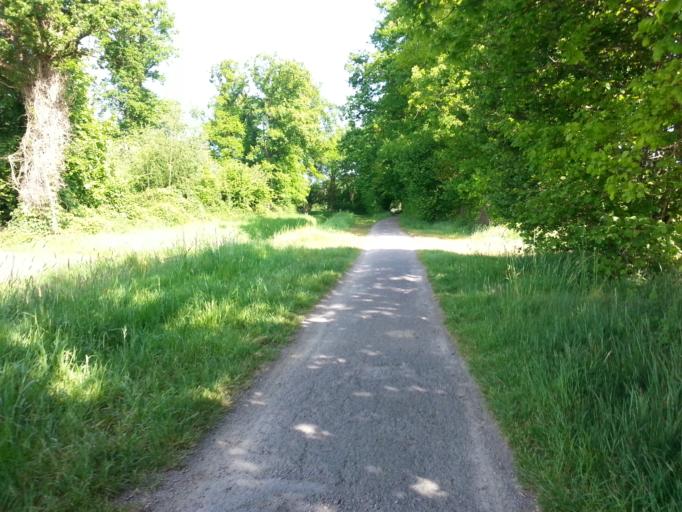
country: NL
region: Gelderland
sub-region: Berkelland
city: Neede
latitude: 52.1225
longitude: 6.6312
